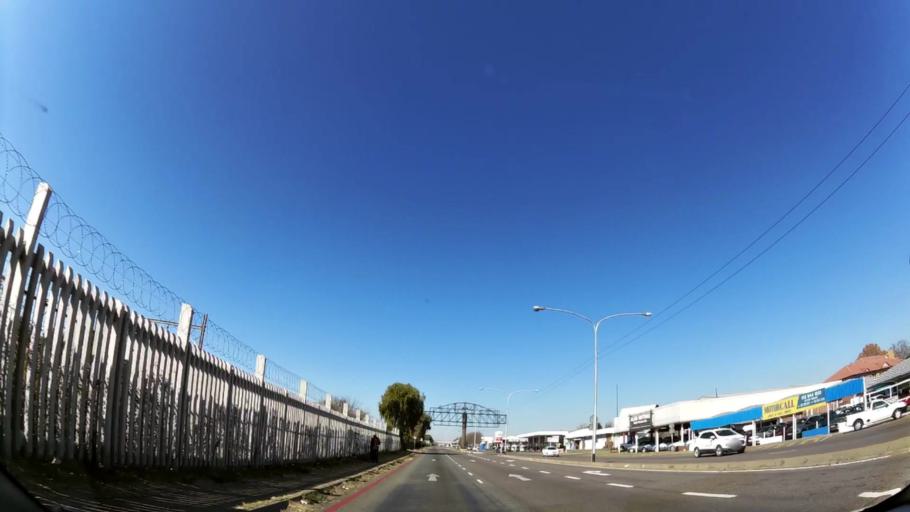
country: ZA
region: Gauteng
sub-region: City of Tshwane Metropolitan Municipality
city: Centurion
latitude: -25.8316
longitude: 28.2086
